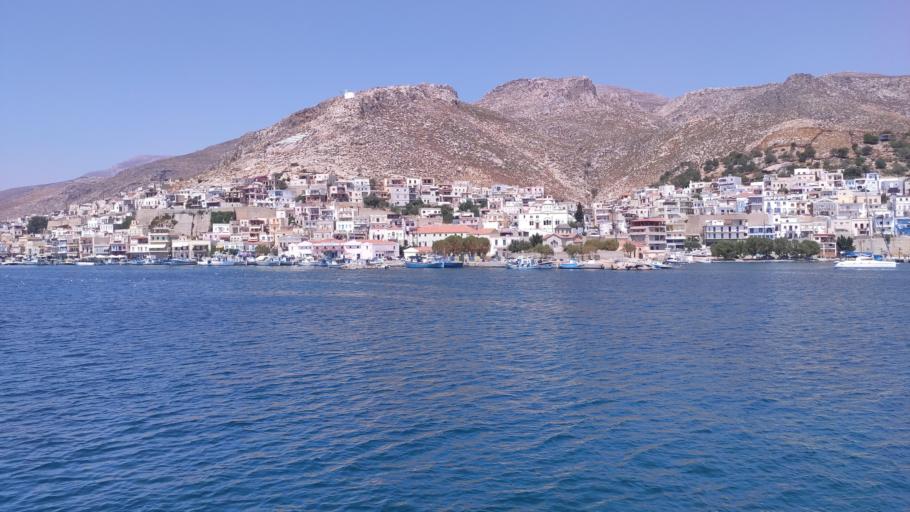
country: GR
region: South Aegean
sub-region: Nomos Dodekanisou
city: Kalymnos
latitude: 36.9490
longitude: 26.9901
